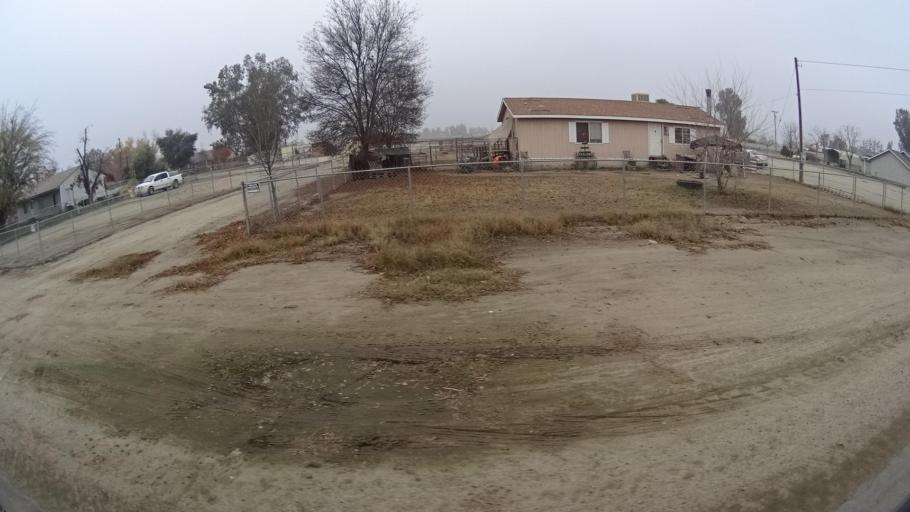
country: US
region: California
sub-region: Kern County
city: Greenfield
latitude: 35.2380
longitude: -119.0803
